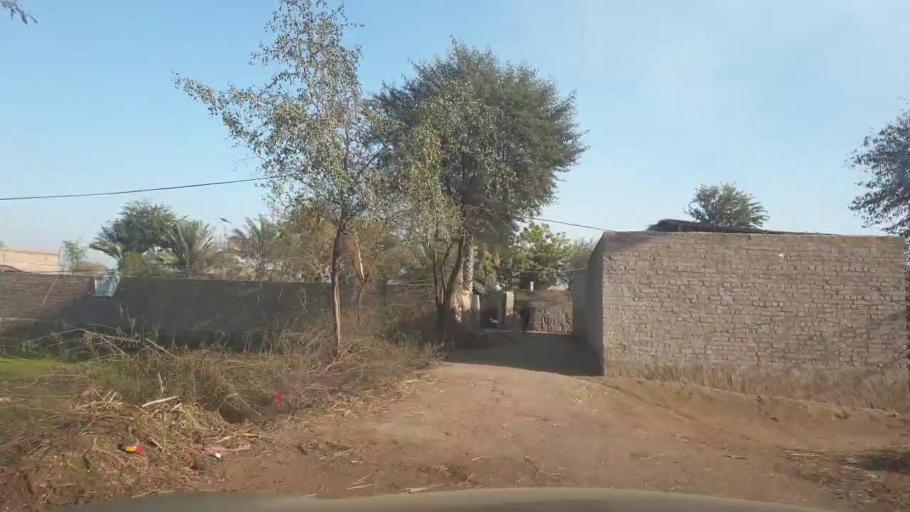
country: PK
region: Sindh
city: Ghotki
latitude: 28.0726
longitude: 69.3778
